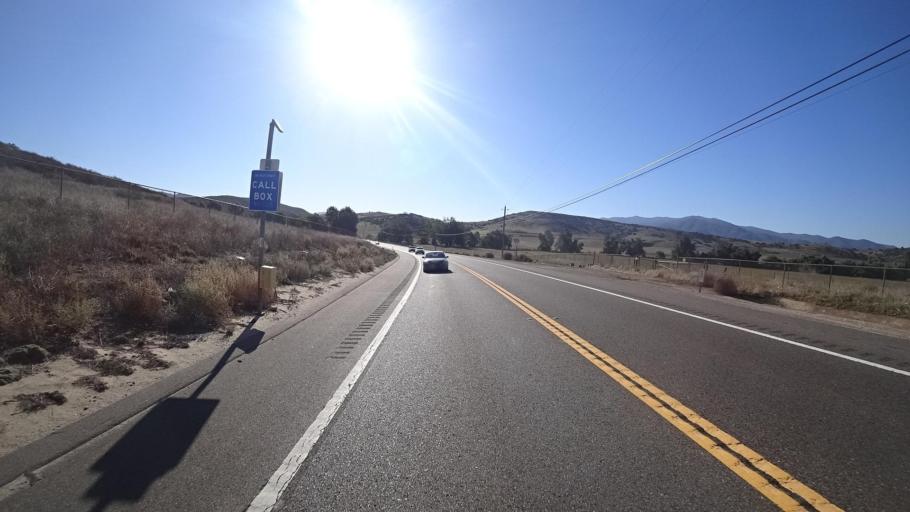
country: US
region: California
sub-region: San Diego County
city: Jamul
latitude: 32.6859
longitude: -116.8497
